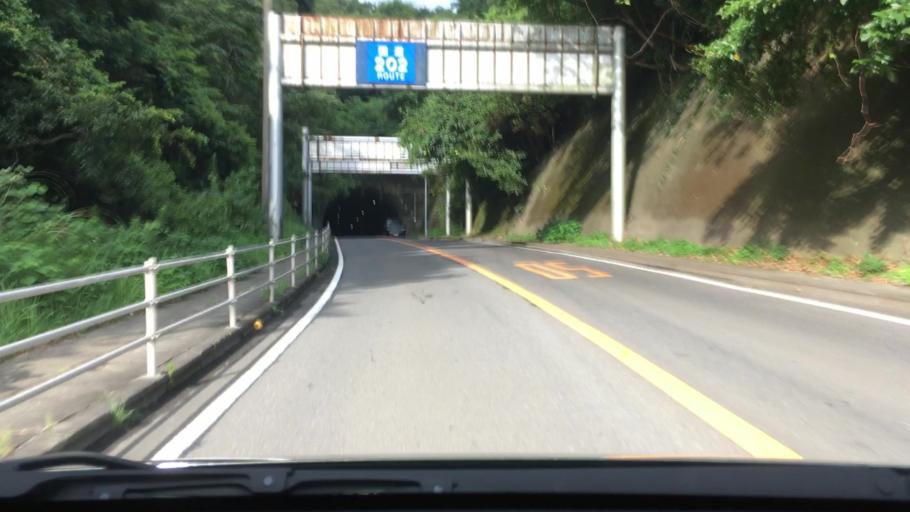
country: JP
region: Nagasaki
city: Togitsu
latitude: 32.8263
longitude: 129.7680
